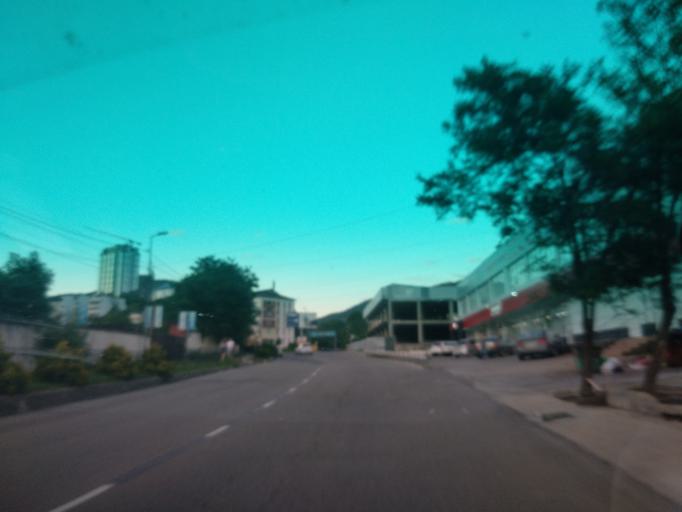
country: RU
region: Krasnodarskiy
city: Tuapse
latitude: 44.1215
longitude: 39.0714
